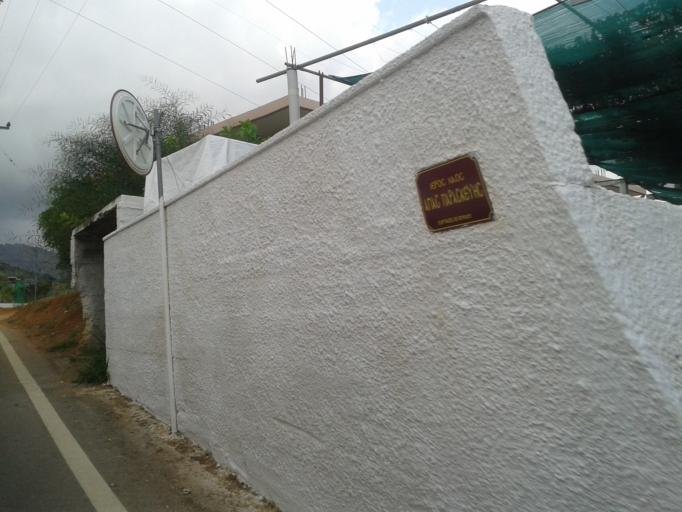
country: GR
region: Crete
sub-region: Nomos Chanias
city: Perivolia
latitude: 35.4781
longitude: 23.9926
